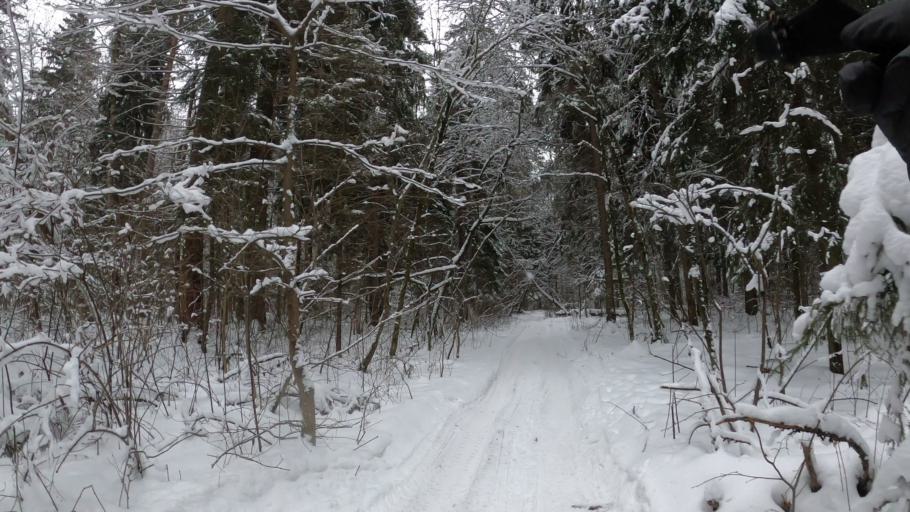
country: RU
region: Moskovskaya
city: Firsanovka
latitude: 55.9332
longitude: 37.2214
